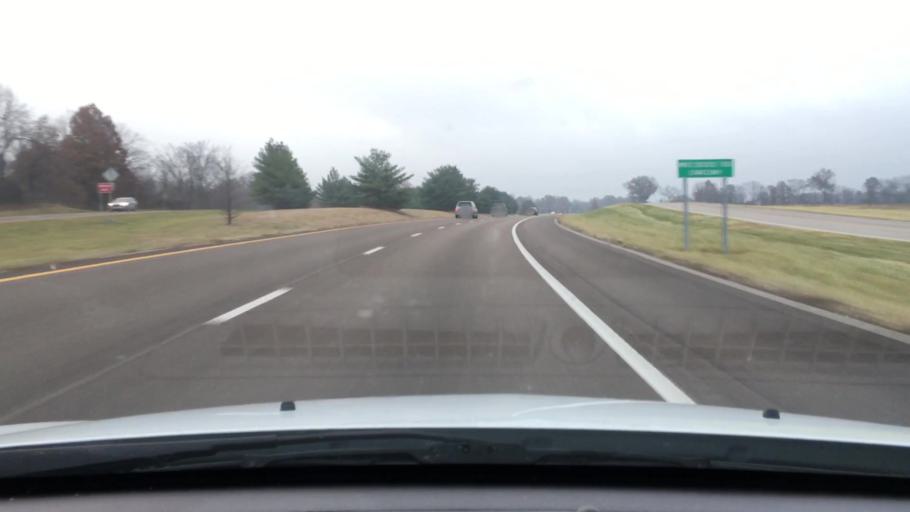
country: US
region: Missouri
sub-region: Callaway County
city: Fulton
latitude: 38.9533
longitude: -91.9379
